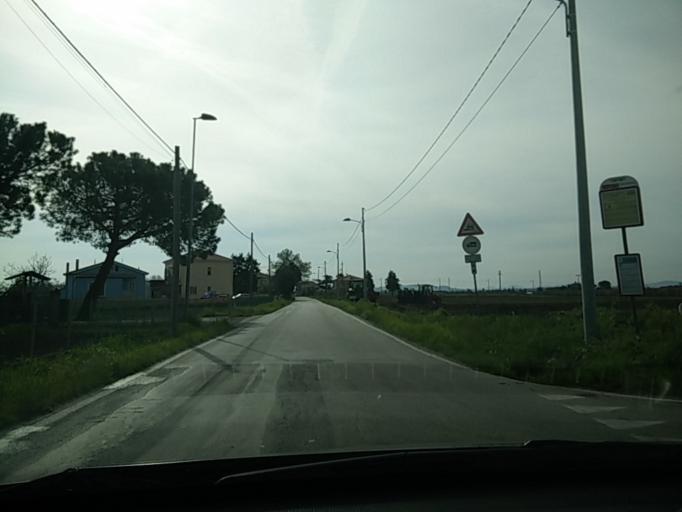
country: IT
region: Emilia-Romagna
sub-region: Provincia di Rimini
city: Santa Giustina
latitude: 44.0841
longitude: 12.4868
